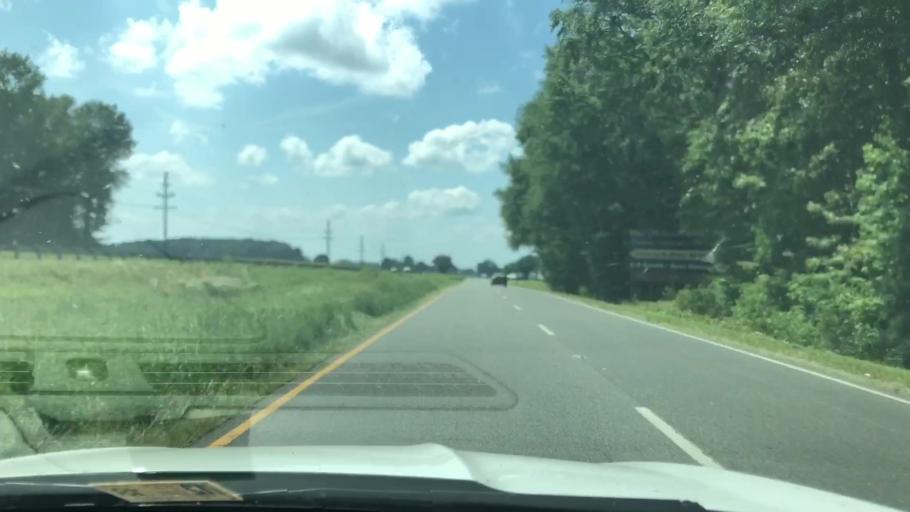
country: US
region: Virginia
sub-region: Richmond County
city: Warsaw
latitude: 37.9622
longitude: -76.8060
